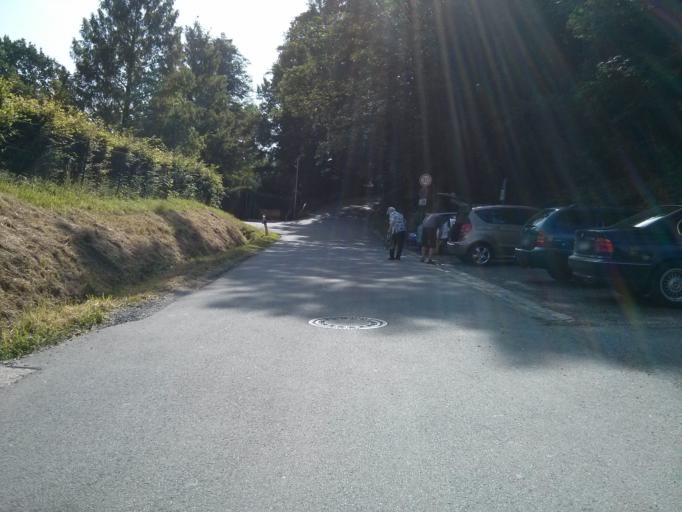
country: DE
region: Bavaria
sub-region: Lower Bavaria
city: Deggendorf
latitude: 48.8286
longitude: 12.9656
